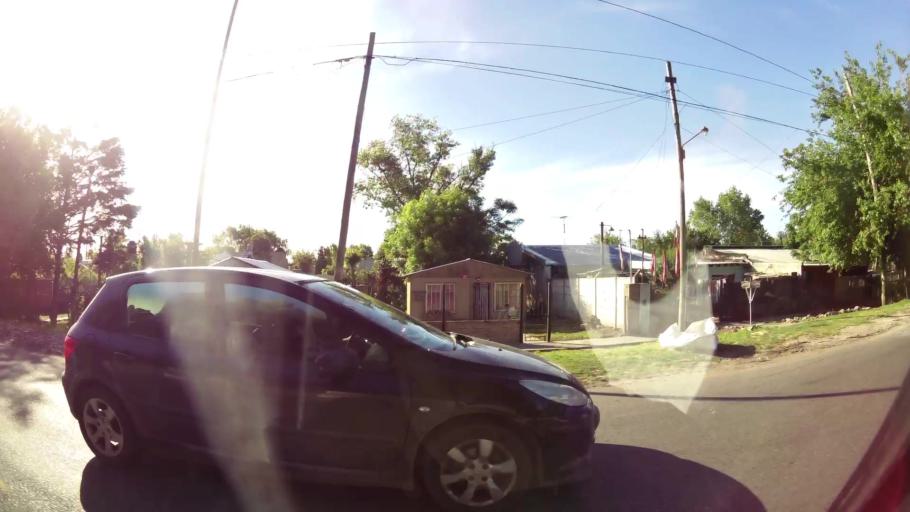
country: AR
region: Buenos Aires
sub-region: Partido de Almirante Brown
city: Adrogue
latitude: -34.8140
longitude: -58.3480
